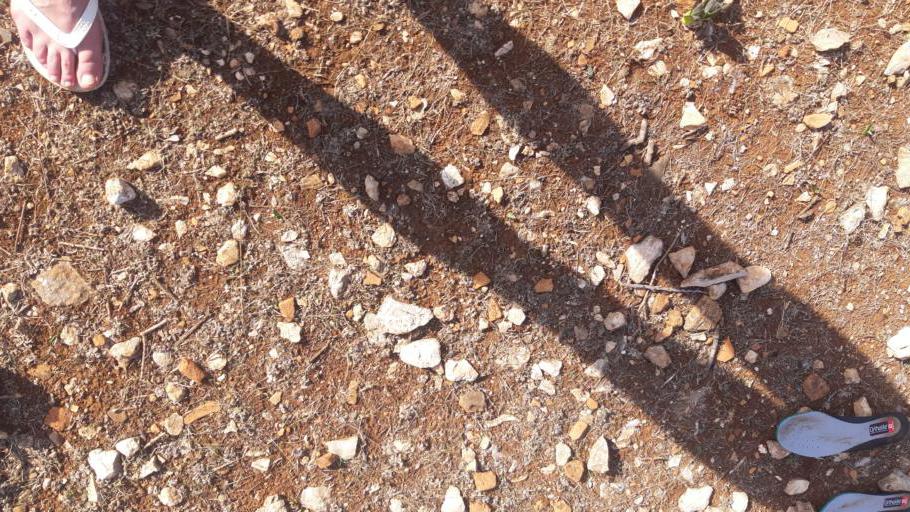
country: TR
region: Antalya
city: Kas
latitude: 36.1590
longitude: 29.7847
